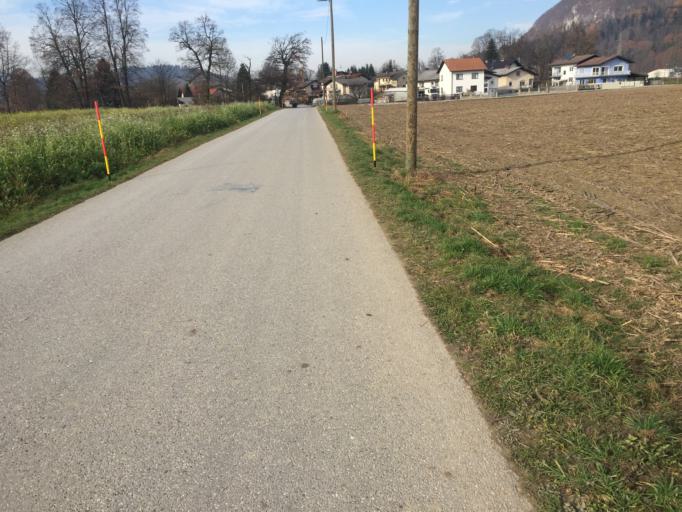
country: SI
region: Medvode
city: Zgornje Pirnice
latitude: 46.1137
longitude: 14.4558
